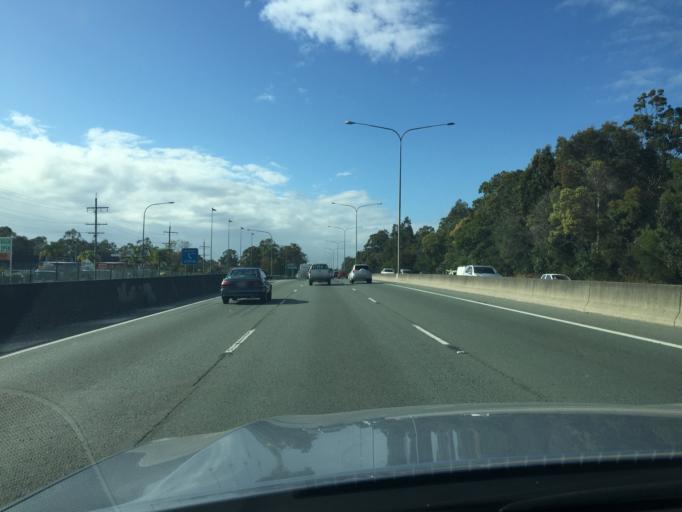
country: AU
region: Queensland
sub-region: Logan
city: Slacks Creek
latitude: -27.6682
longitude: 153.1766
